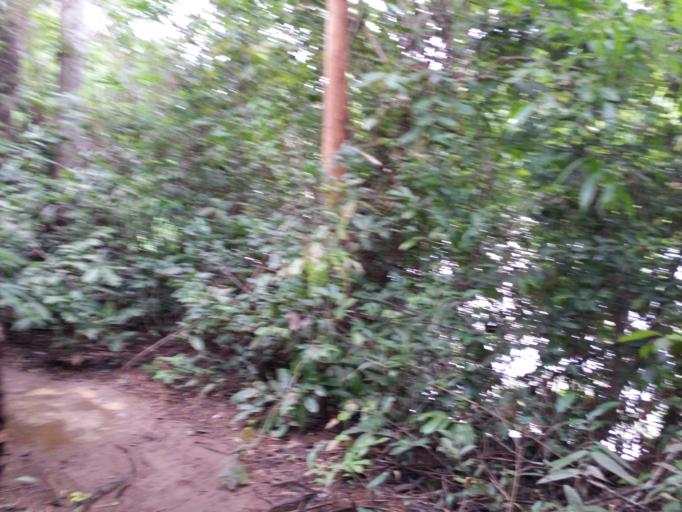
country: LA
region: Xekong
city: Thateng
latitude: 15.5272
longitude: 106.2725
